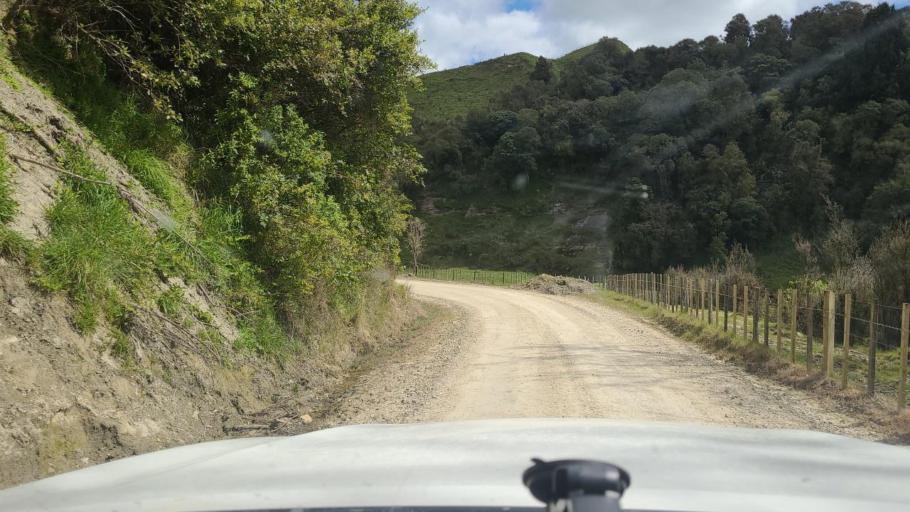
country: NZ
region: Gisborne
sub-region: Gisborne District
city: Gisborne
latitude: -38.8275
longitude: 177.7293
